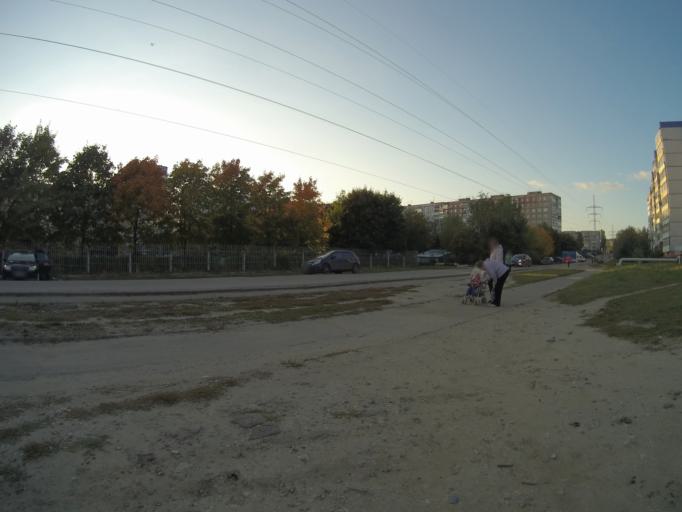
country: RU
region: Vladimir
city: Vladimir
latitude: 56.1072
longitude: 40.3490
